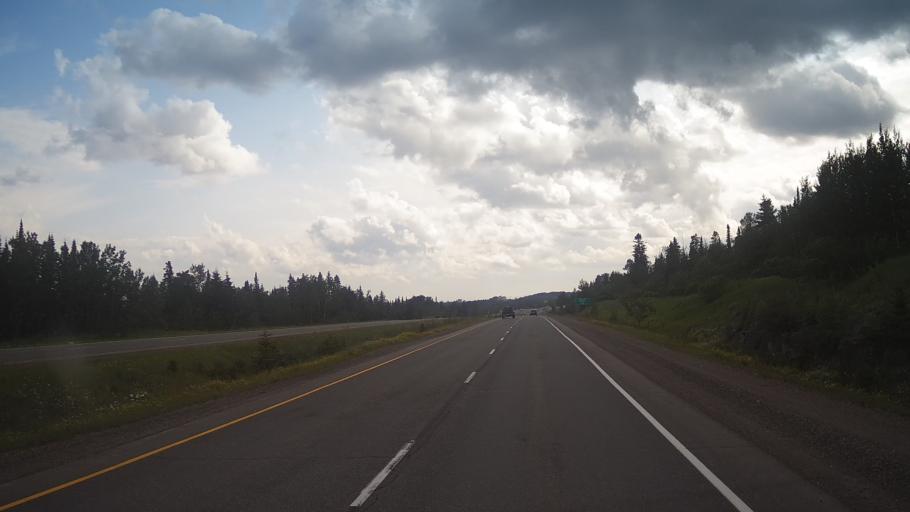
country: CA
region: Ontario
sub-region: Thunder Bay District
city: Thunder Bay
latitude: 48.4678
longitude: -89.2144
